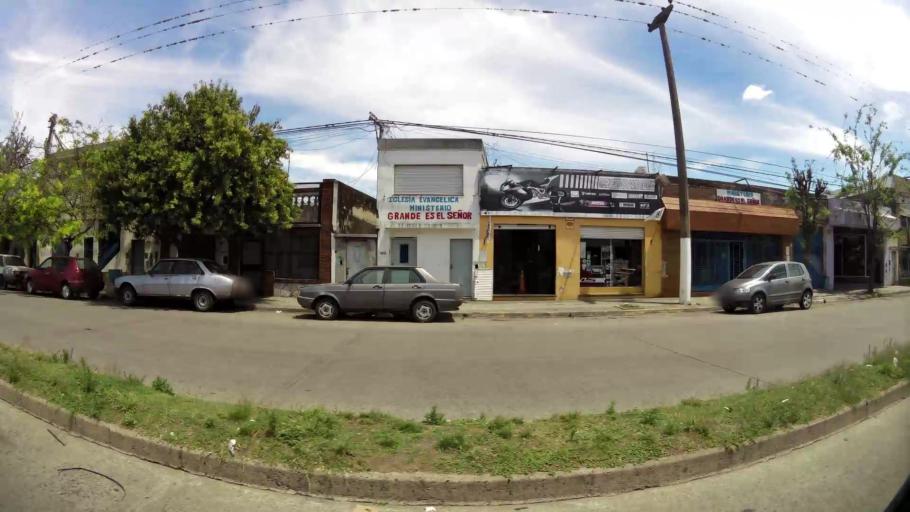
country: AR
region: Santa Fe
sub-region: Departamento de Rosario
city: Rosario
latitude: -32.9877
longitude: -60.6284
